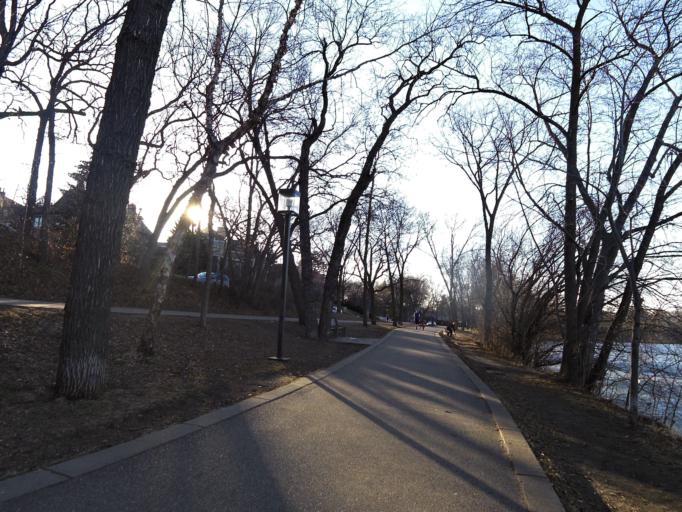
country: US
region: Minnesota
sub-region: Hennepin County
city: Richfield
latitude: 44.9162
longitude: -93.3108
